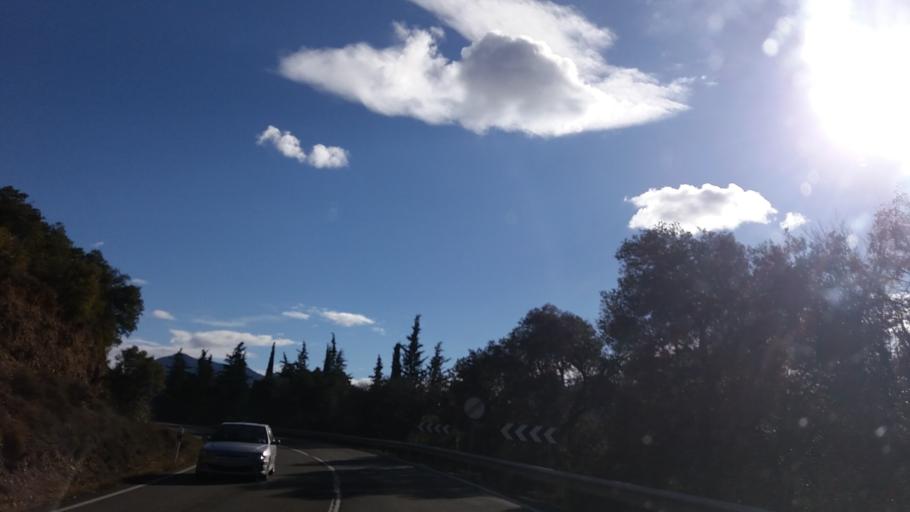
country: ES
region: Aragon
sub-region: Provincia de Huesca
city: Bailo
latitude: 42.5714
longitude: -0.8175
